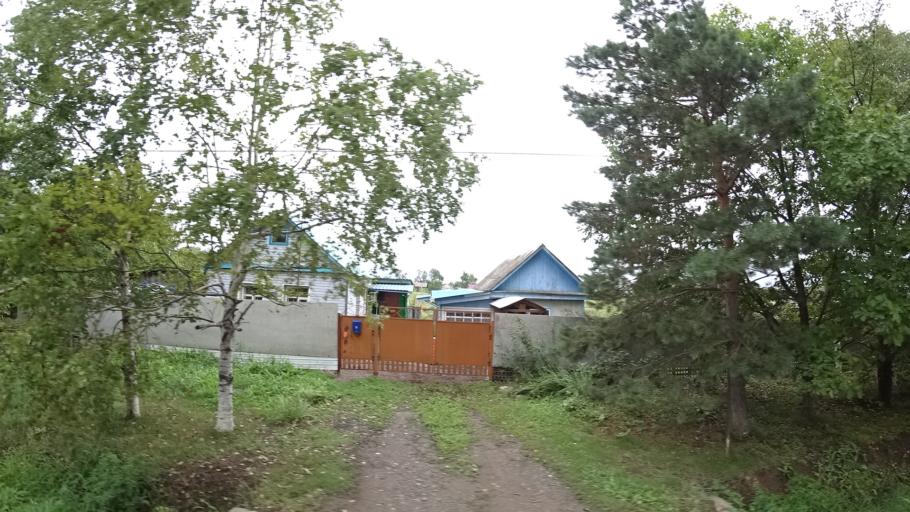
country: RU
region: Primorskiy
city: Chernigovka
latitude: 44.3348
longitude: 132.5630
